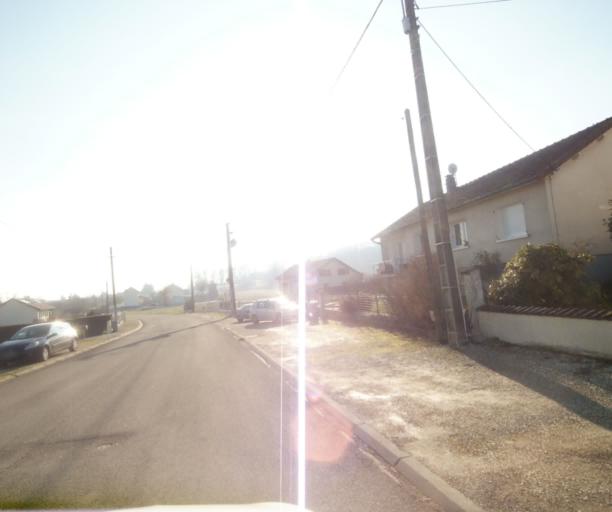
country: FR
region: Champagne-Ardenne
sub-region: Departement de la Haute-Marne
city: Wassy
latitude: 48.5127
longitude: 4.9173
